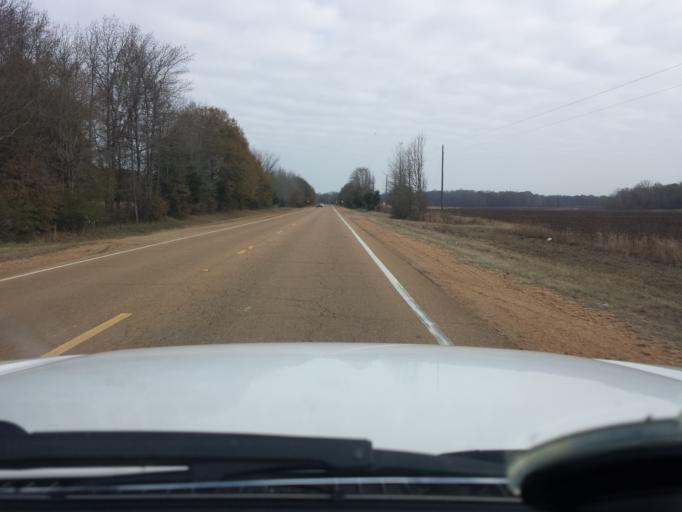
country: US
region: Mississippi
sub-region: Yazoo County
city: Yazoo City
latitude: 32.8008
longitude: -90.2248
